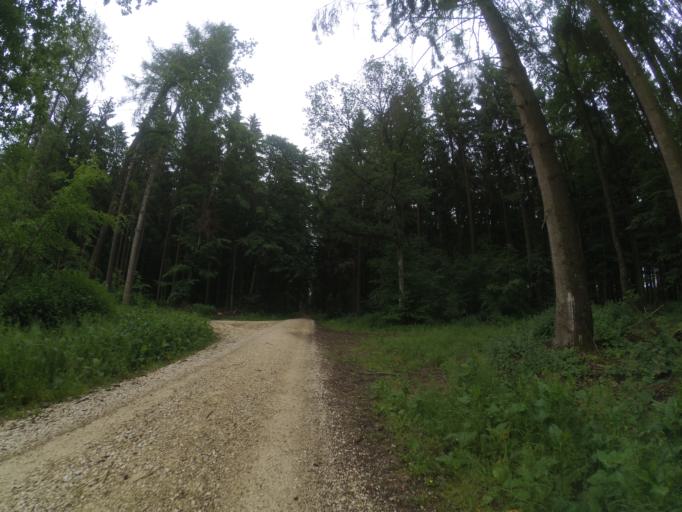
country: DE
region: Baden-Wuerttemberg
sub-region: Tuebingen Region
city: Borslingen
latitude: 48.5140
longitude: 10.0618
